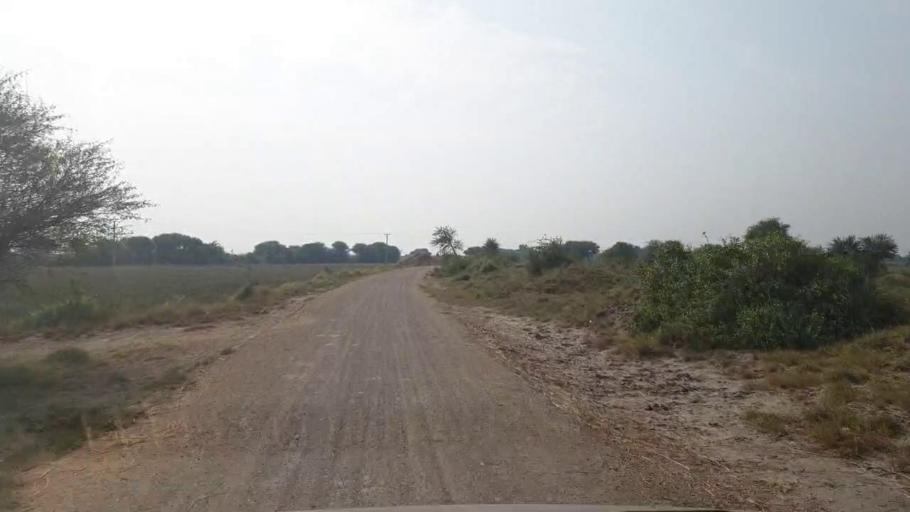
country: PK
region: Sindh
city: Tando Muhammad Khan
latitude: 25.1129
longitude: 68.4959
